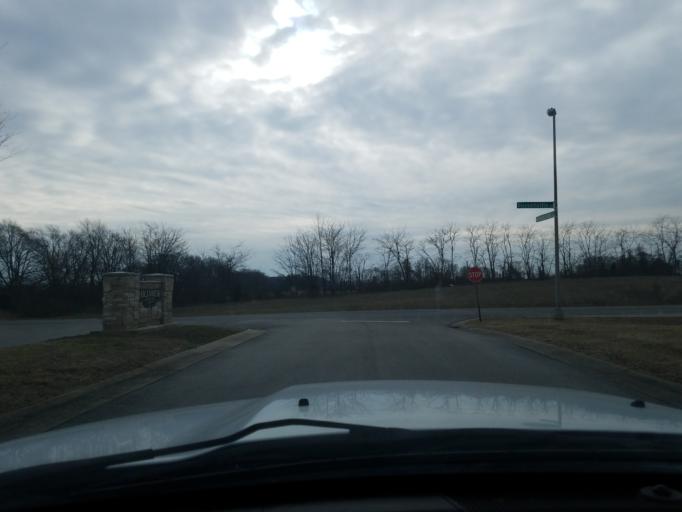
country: US
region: Kentucky
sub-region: Warren County
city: Bowling Green
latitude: 36.9523
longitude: -86.5124
